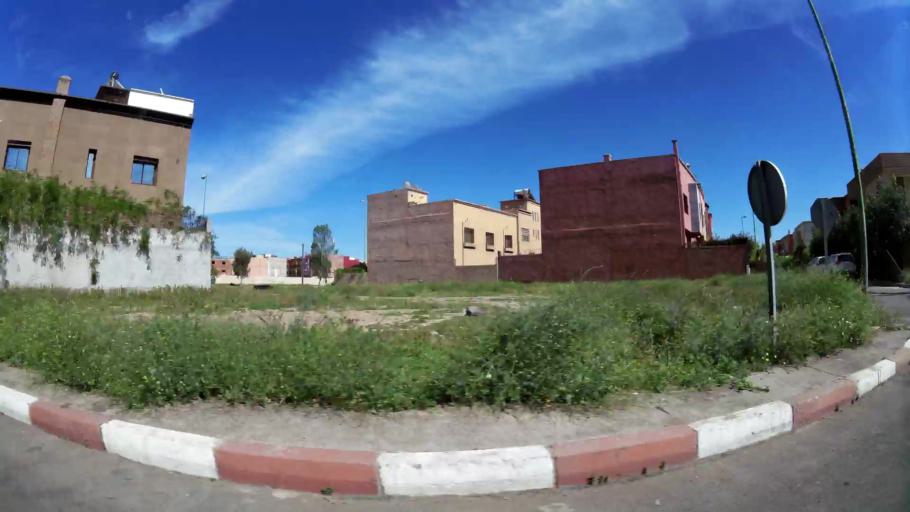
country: MA
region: Marrakech-Tensift-Al Haouz
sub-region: Marrakech
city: Marrakesh
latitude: 31.6411
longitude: -8.0421
